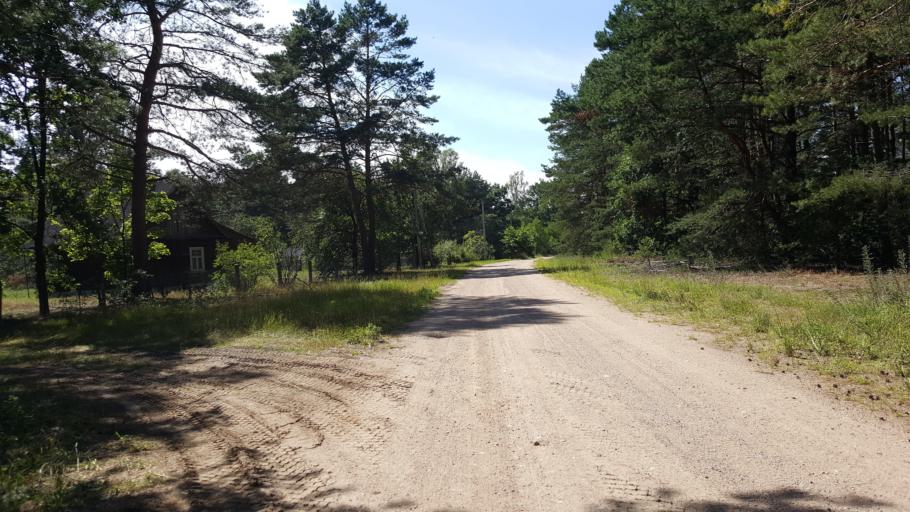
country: BY
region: Brest
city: Zhabinka
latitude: 52.4603
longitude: 24.1178
